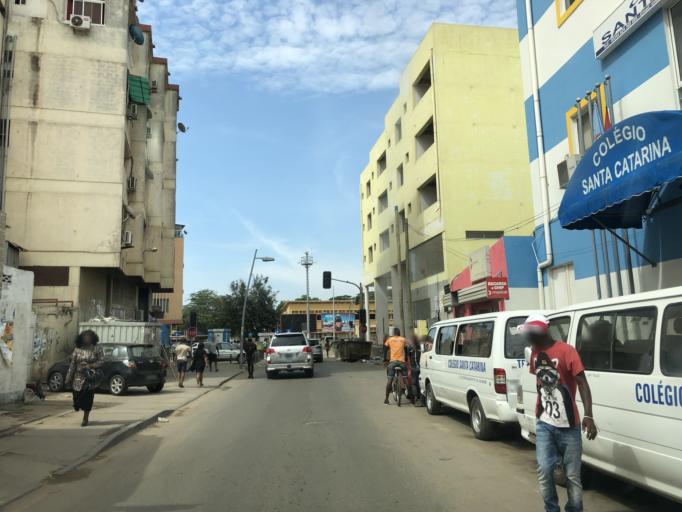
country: AO
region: Luanda
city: Luanda
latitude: -8.8200
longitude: 13.2527
